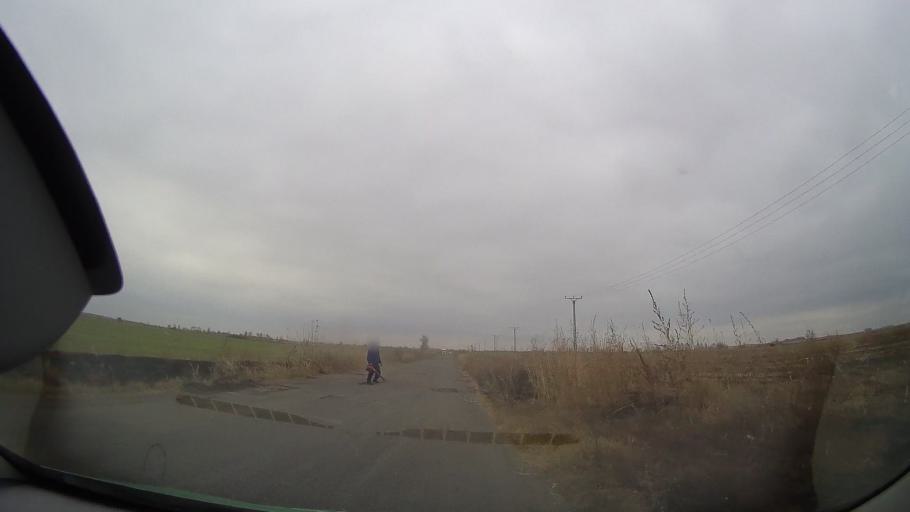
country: RO
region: Braila
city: Dudesti
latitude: 44.9277
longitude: 27.4278
